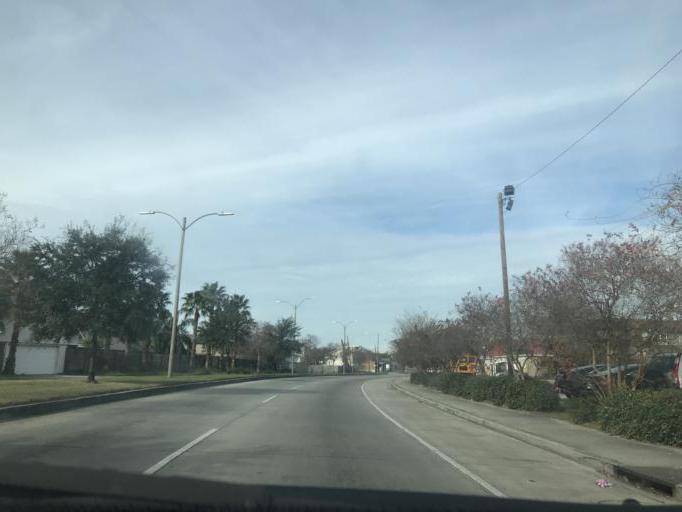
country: US
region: Louisiana
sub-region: Orleans Parish
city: New Orleans
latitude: 29.9570
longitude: -90.1068
